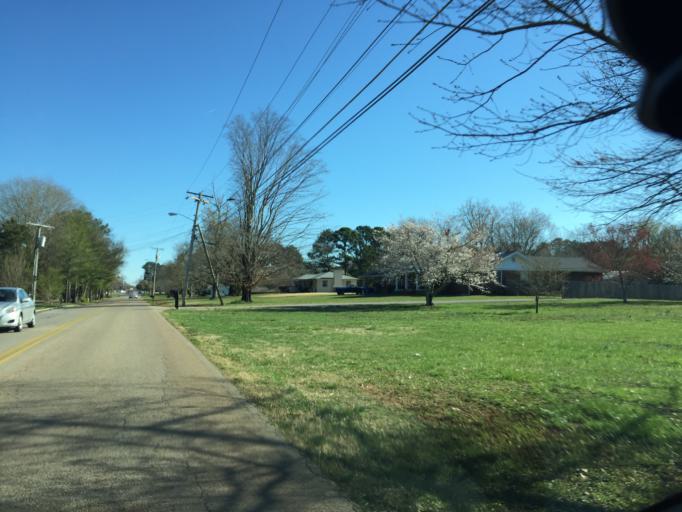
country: US
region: Tennessee
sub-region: Hamilton County
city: East Brainerd
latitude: 35.0374
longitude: -85.1711
